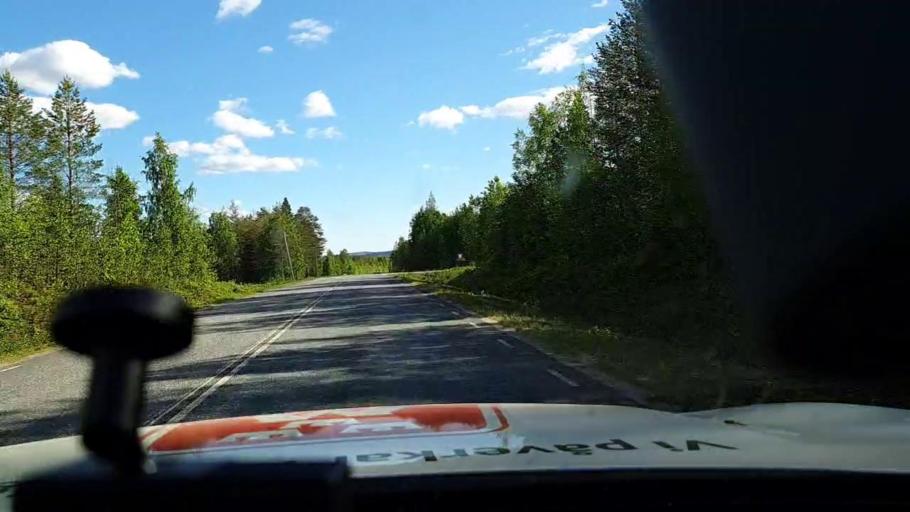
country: SE
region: Norrbotten
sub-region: Overtornea Kommun
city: OEvertornea
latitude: 66.3491
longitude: 23.6480
